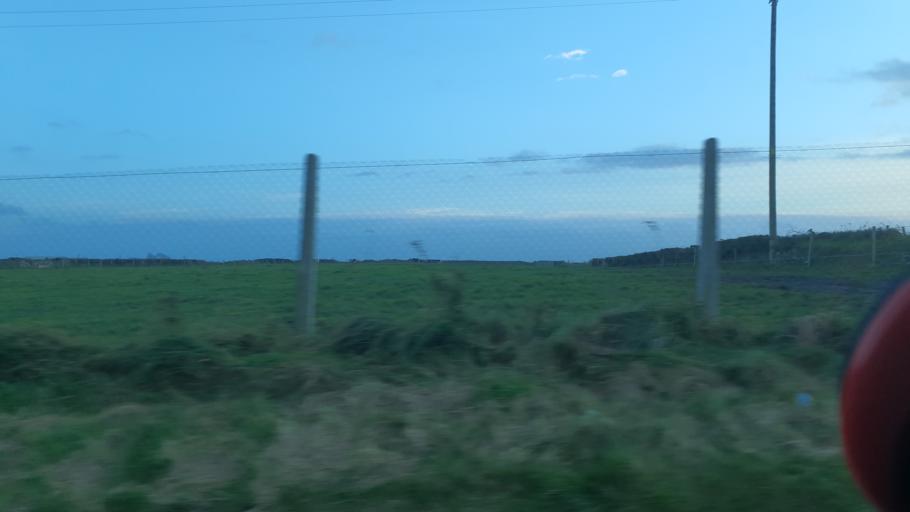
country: GB
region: Northern Ireland
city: Kilkeel
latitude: 54.0390
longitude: -6.0896
